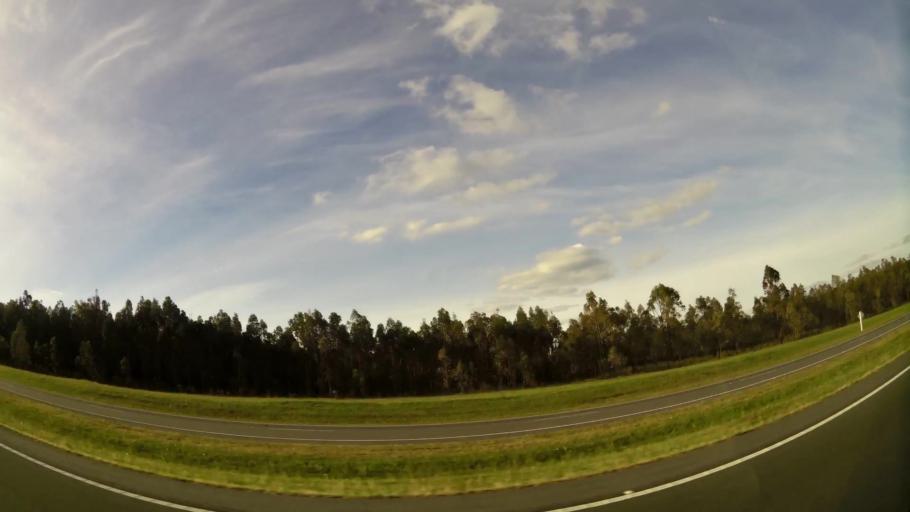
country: UY
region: Maldonado
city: Pan de Azucar
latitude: -34.7910
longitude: -55.3105
